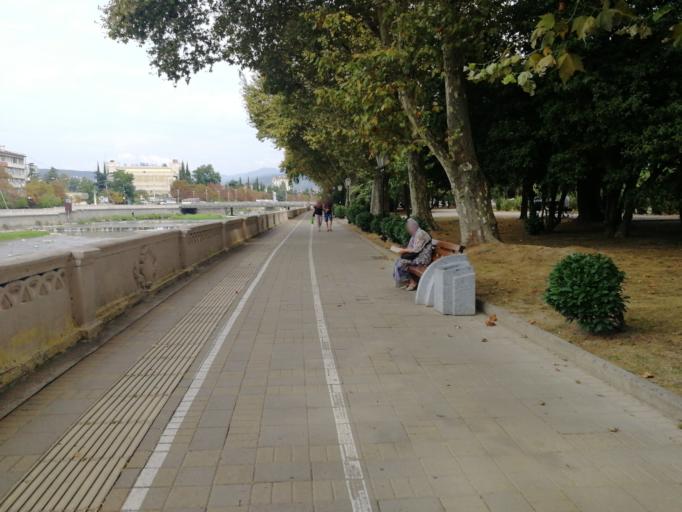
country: RU
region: Krasnodarskiy
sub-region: Sochi City
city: Sochi
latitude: 43.5924
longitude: 39.7201
